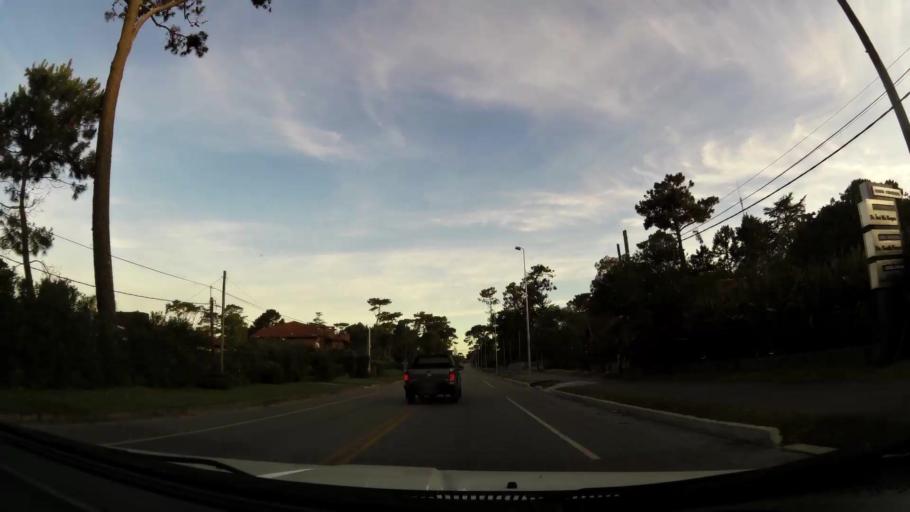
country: UY
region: Maldonado
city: Maldonado
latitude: -34.9205
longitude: -54.9467
